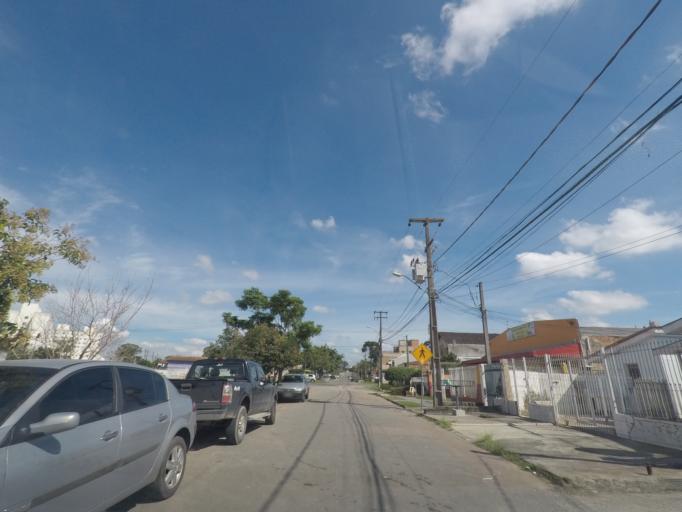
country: BR
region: Parana
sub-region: Curitiba
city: Curitiba
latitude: -25.4779
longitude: -49.2705
